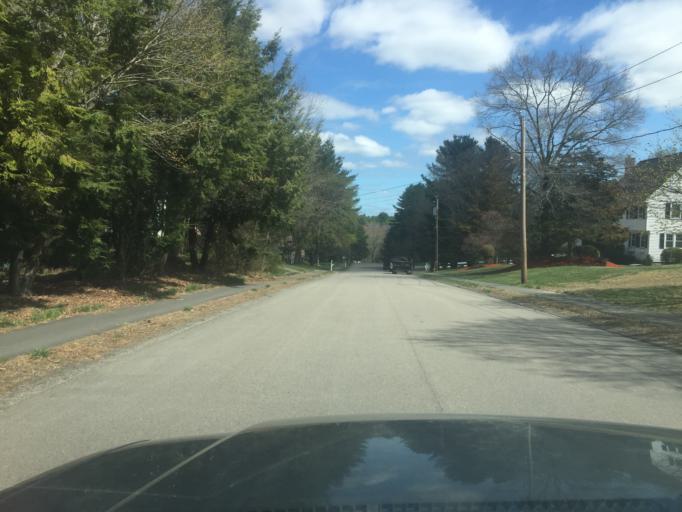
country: US
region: Massachusetts
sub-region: Norfolk County
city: Medway
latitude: 42.1662
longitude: -71.4035
